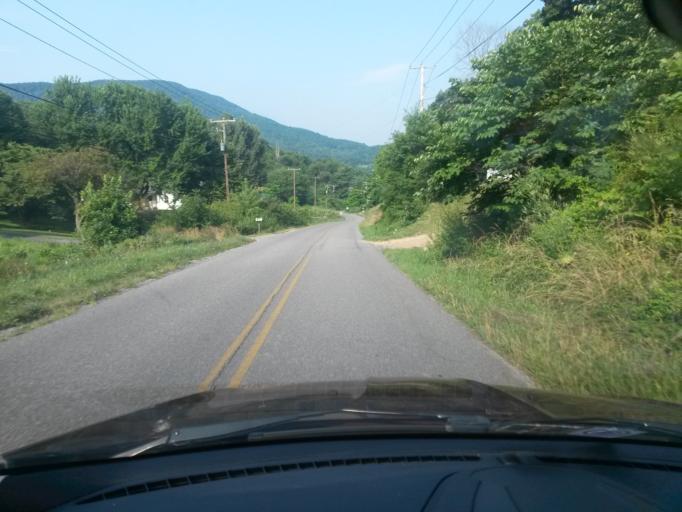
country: US
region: Virginia
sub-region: Giles County
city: Narrows
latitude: 37.3694
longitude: -80.8076
